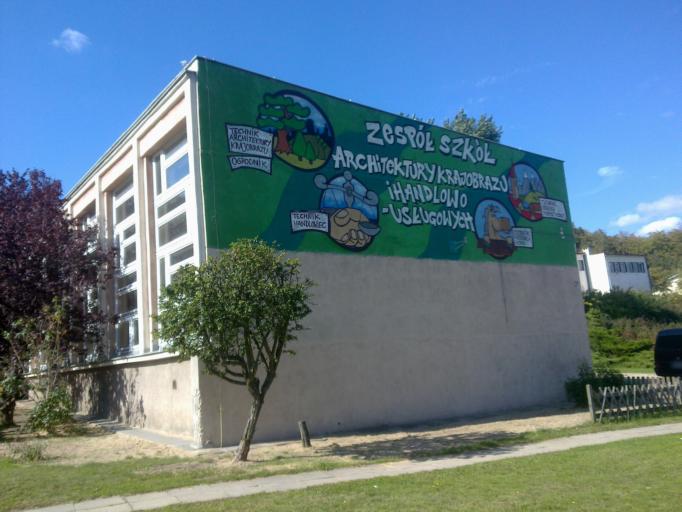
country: PL
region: Pomeranian Voivodeship
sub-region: Sopot
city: Sopot
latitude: 54.4217
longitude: 18.5615
